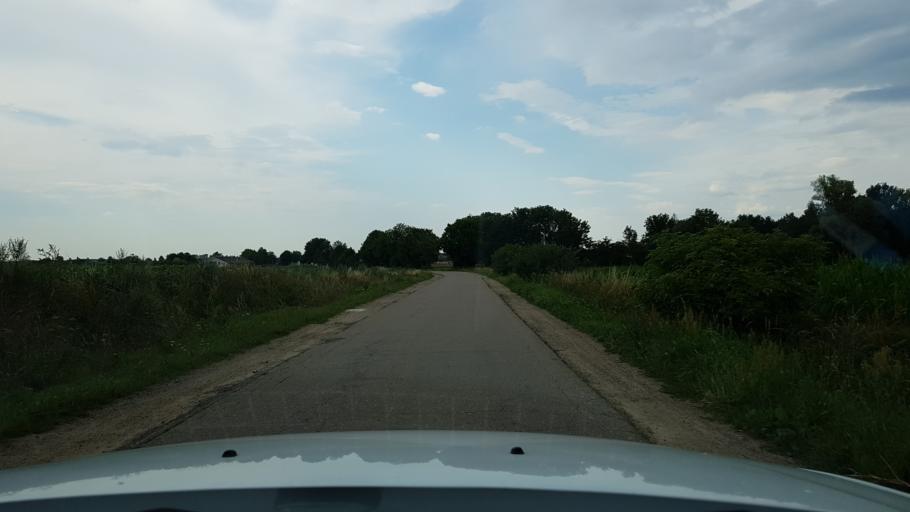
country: PL
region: West Pomeranian Voivodeship
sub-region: Powiat walecki
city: Walcz
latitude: 53.3644
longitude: 16.3426
